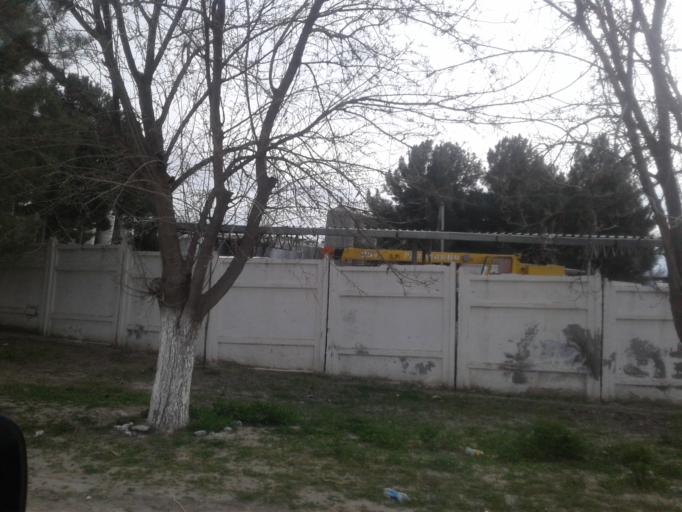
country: TM
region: Ahal
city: Abadan
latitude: 38.1242
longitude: 58.3472
